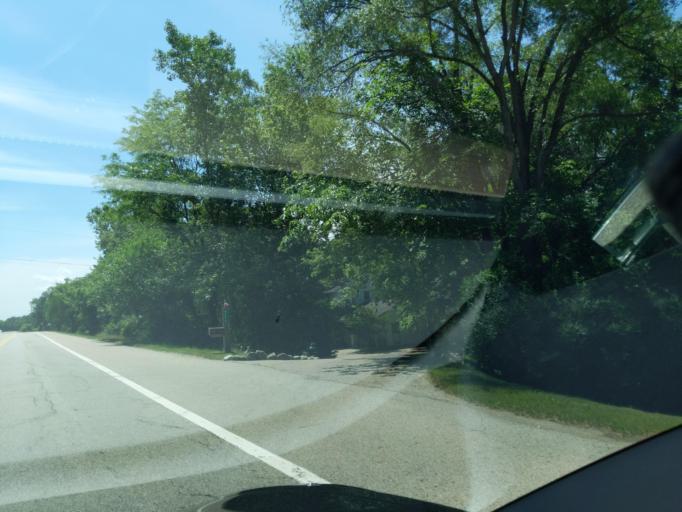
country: US
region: Michigan
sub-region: Kent County
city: Forest Hills
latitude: 42.9478
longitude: -85.4605
